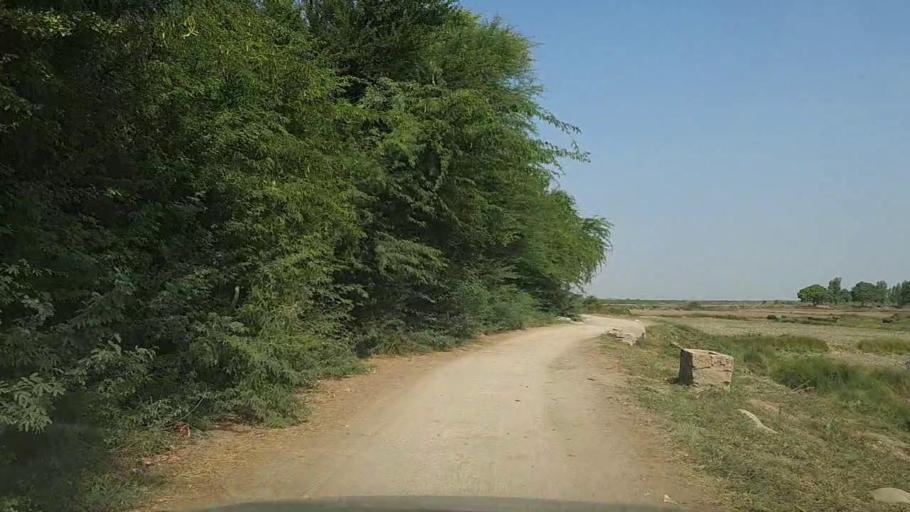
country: PK
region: Sindh
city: Thatta
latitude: 24.6198
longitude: 67.9609
